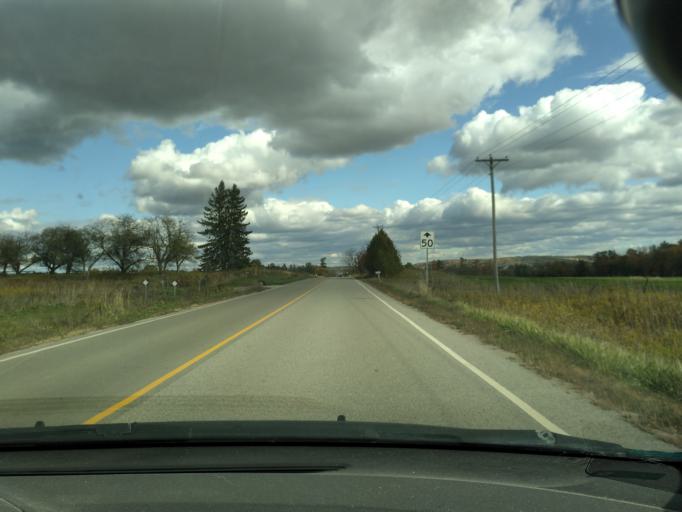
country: CA
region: Ontario
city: Bradford West Gwillimbury
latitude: 44.0837
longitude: -79.5863
